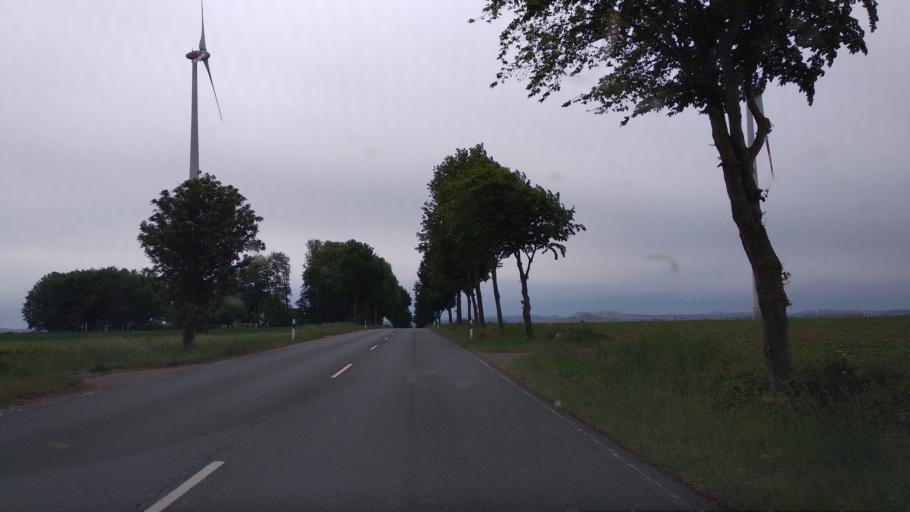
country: DE
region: North Rhine-Westphalia
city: Borgentreich
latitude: 51.5858
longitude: 9.1526
